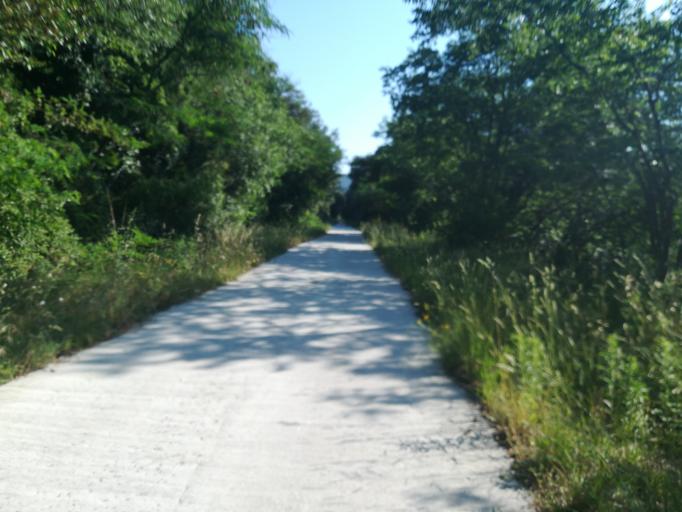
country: FR
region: Languedoc-Roussillon
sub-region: Departement des Pyrenees-Orientales
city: Reiners
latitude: 42.4905
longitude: 2.7012
